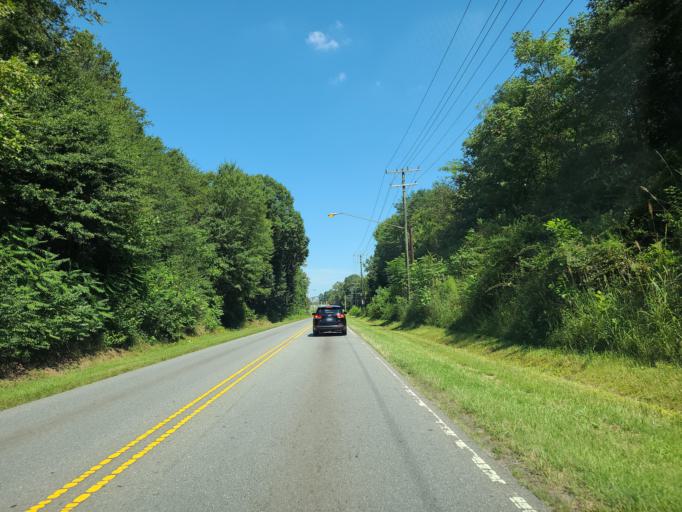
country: US
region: North Carolina
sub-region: Lincoln County
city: Lincolnton
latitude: 35.4648
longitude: -81.2407
